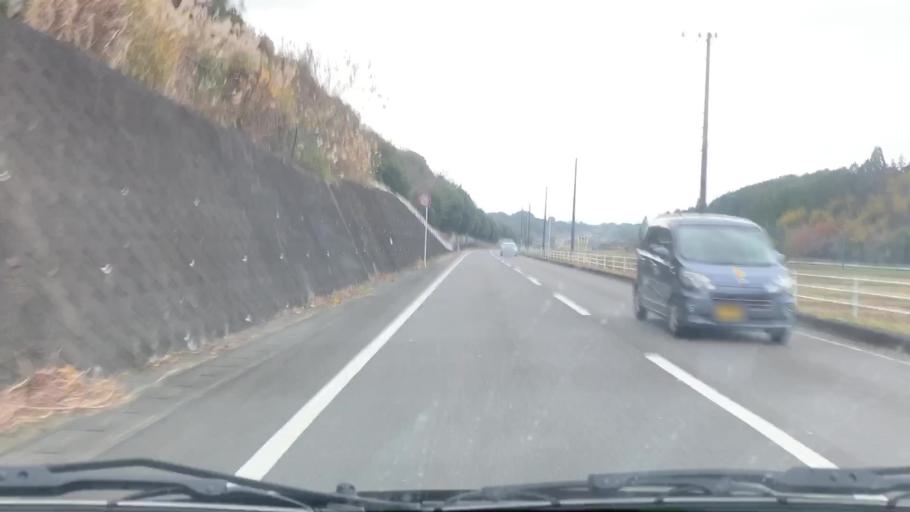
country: JP
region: Saga Prefecture
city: Ureshinomachi-shimojuku
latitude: 33.1200
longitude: 129.9785
